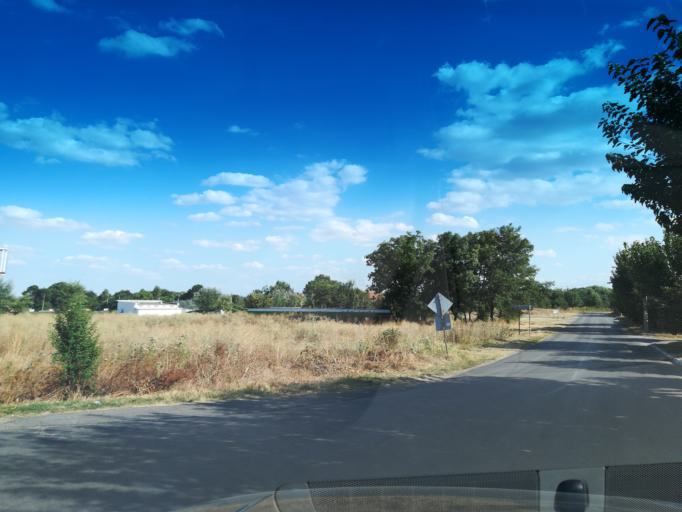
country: BG
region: Khaskovo
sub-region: Obshtina Mineralni Bani
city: Mineralni Bani
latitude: 42.0221
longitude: 25.4301
